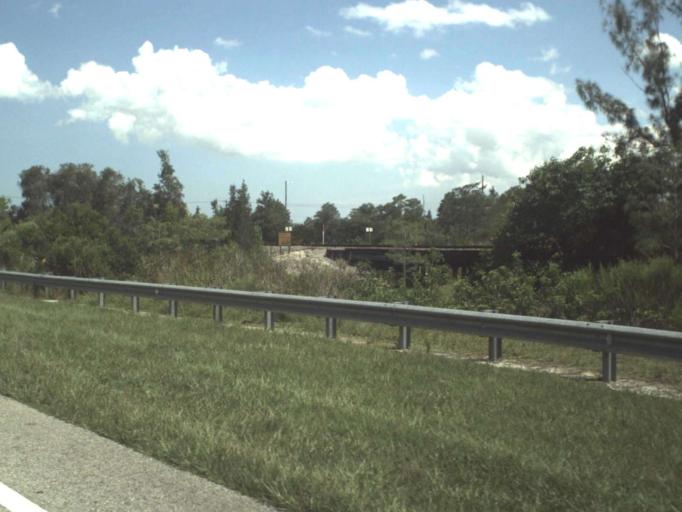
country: US
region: Florida
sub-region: Palm Beach County
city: Palm Beach Gardens
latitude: 26.8124
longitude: -80.1564
